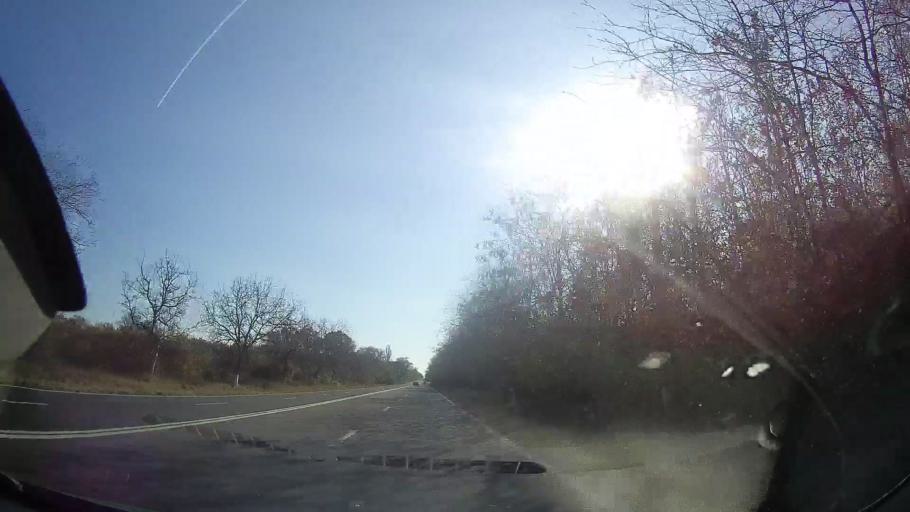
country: RO
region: Constanta
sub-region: Comuna Douazeci si Trei August
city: Dulcesti
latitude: 43.8791
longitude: 28.5736
